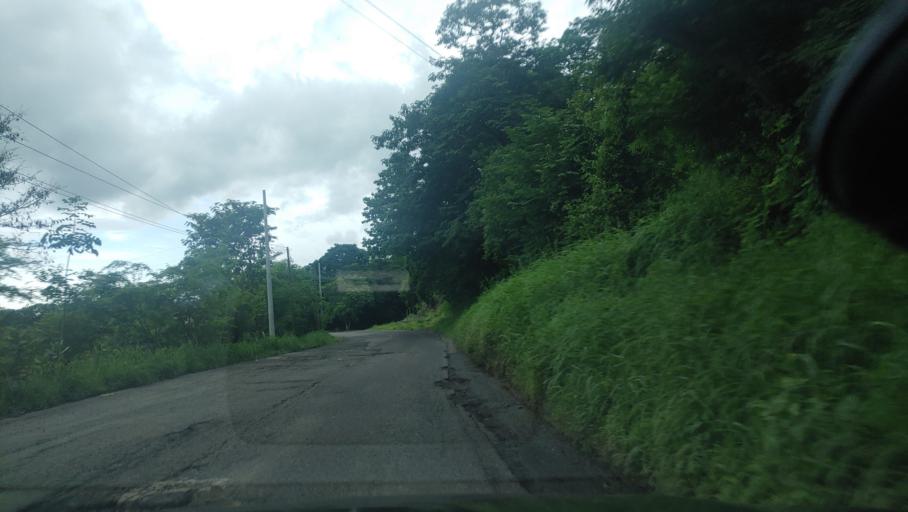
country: HN
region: Choluteca
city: Corpus
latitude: 13.3738
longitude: -87.0439
